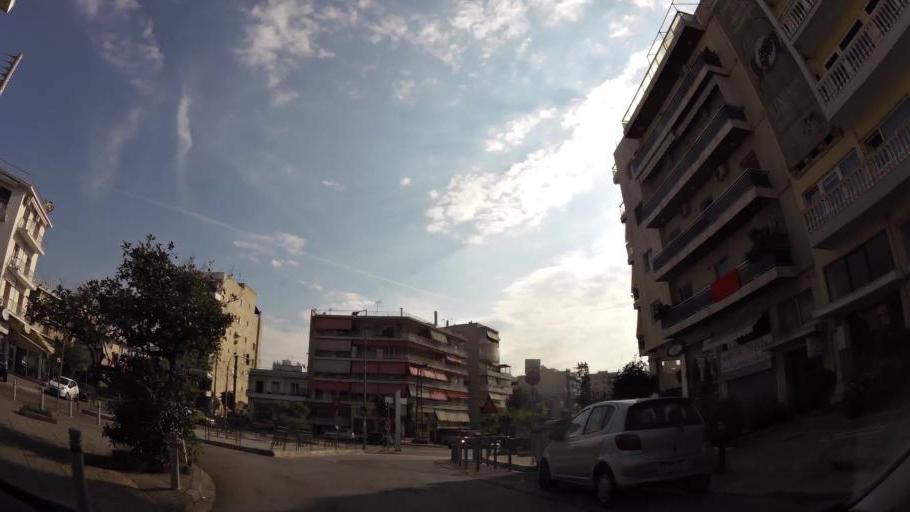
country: GR
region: Attica
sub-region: Nomarchia Athinas
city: Nea Smyrni
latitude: 37.9388
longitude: 23.7122
